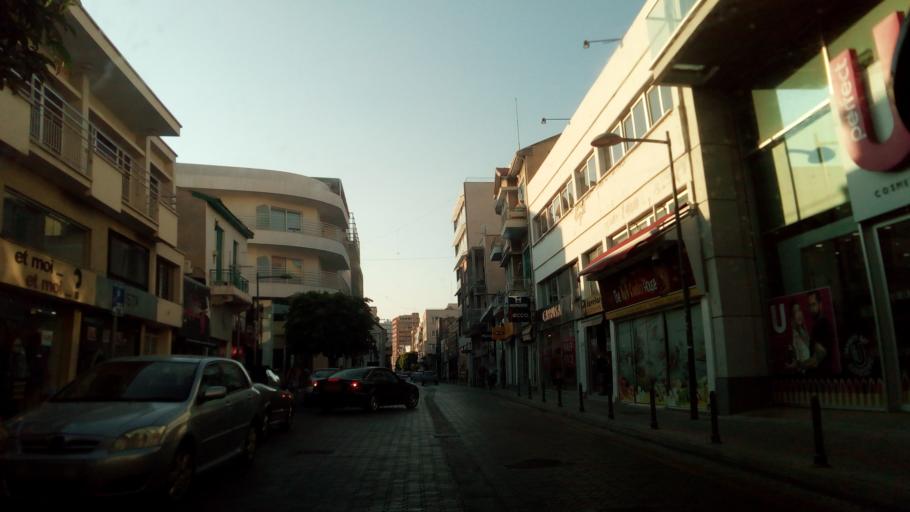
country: CY
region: Limassol
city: Limassol
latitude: 34.6771
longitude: 33.0451
